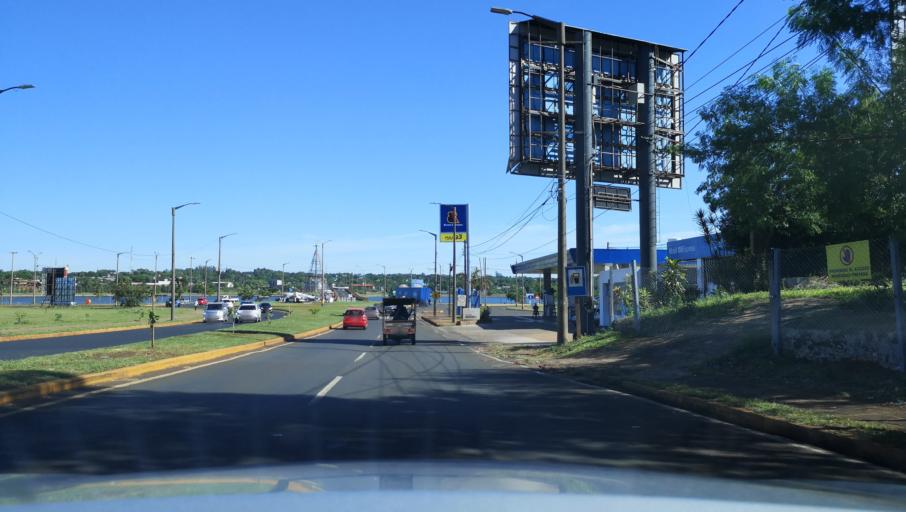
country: PY
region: Itapua
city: Encarnacion
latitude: -27.3231
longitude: -55.8735
